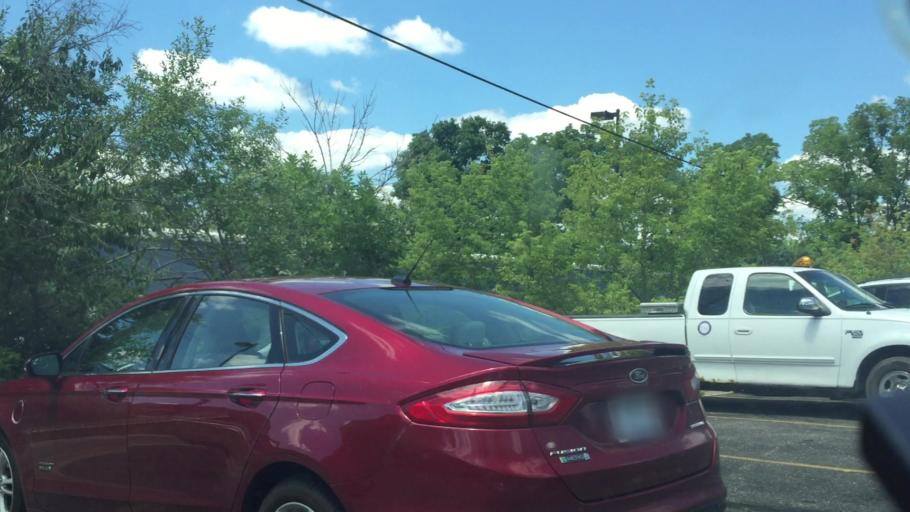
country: US
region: Michigan
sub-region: Washtenaw County
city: Ann Arbor
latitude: 42.2984
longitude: -83.6972
